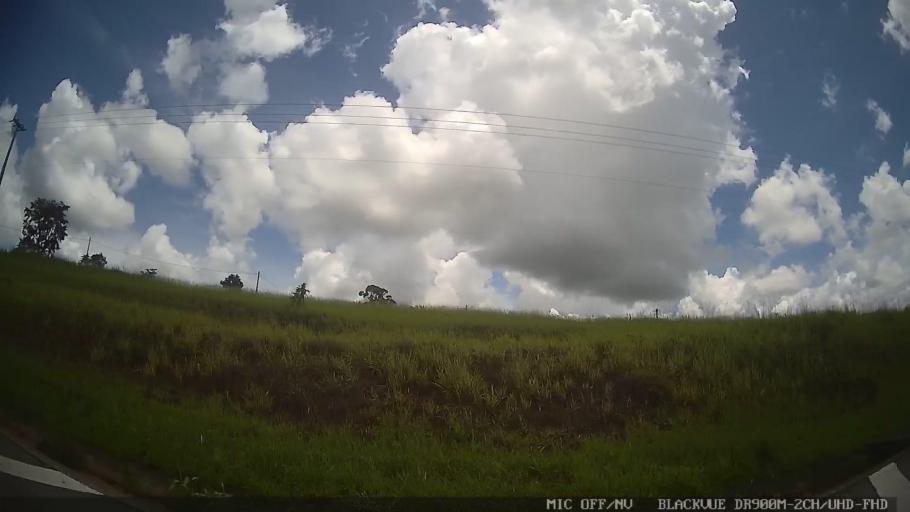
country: BR
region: Sao Paulo
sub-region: Braganca Paulista
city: Braganca Paulista
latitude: -22.8612
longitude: -46.6332
